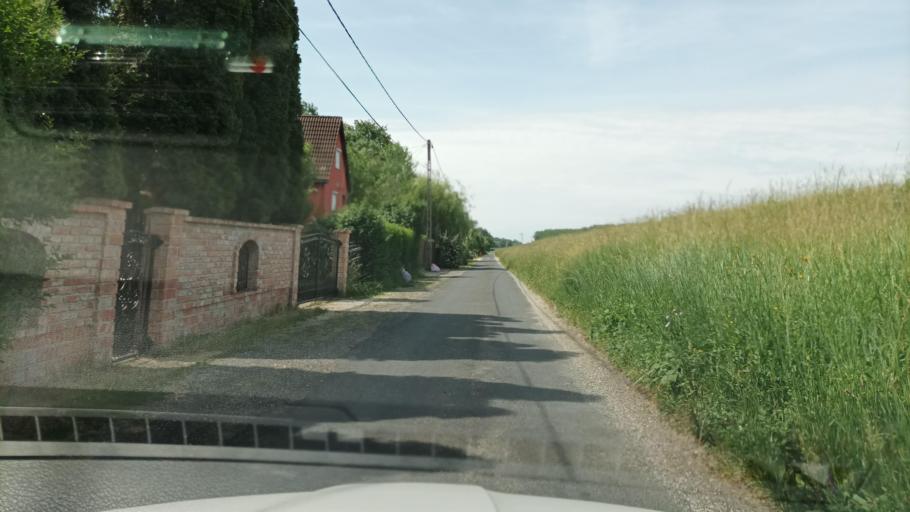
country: HU
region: Pest
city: Domsod
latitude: 47.1001
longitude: 18.9965
